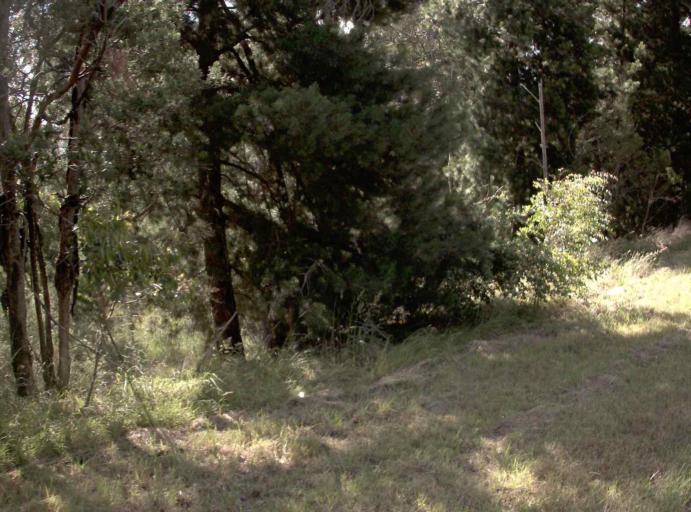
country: AU
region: Victoria
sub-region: Latrobe
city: Morwell
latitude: -38.1849
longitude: 146.4044
